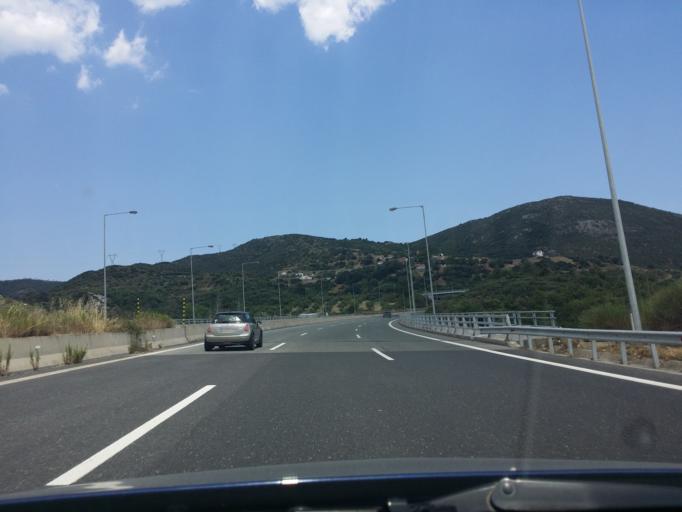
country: GR
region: Peloponnese
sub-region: Nomos Arkadias
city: Megalopoli
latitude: 37.3943
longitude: 22.1780
